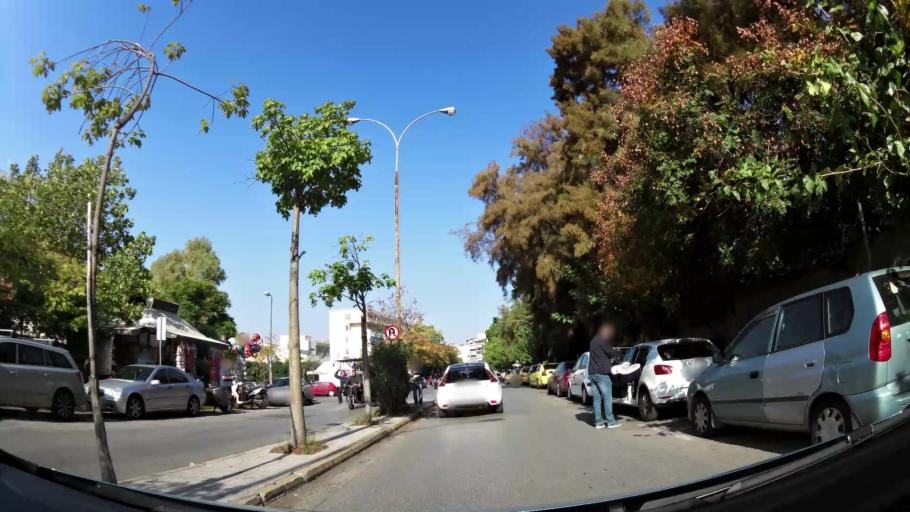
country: GR
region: Attica
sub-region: Nomarchia Athinas
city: Kaisariani
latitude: 37.9840
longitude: 23.7682
